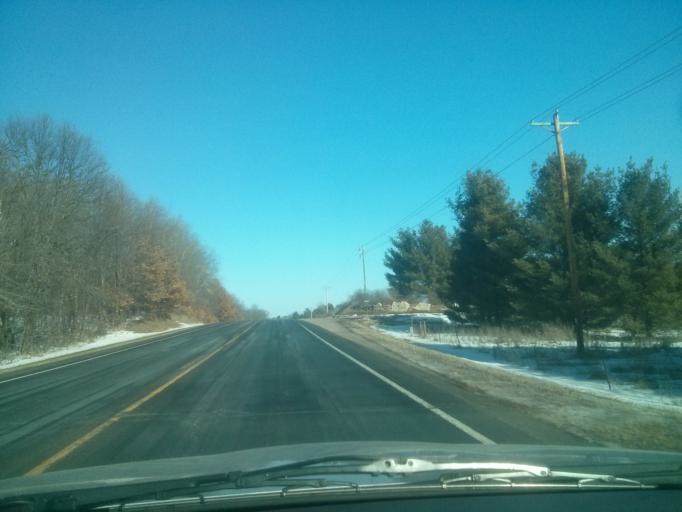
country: US
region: Minnesota
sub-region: Washington County
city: Stillwater
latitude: 45.0820
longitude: -92.7361
